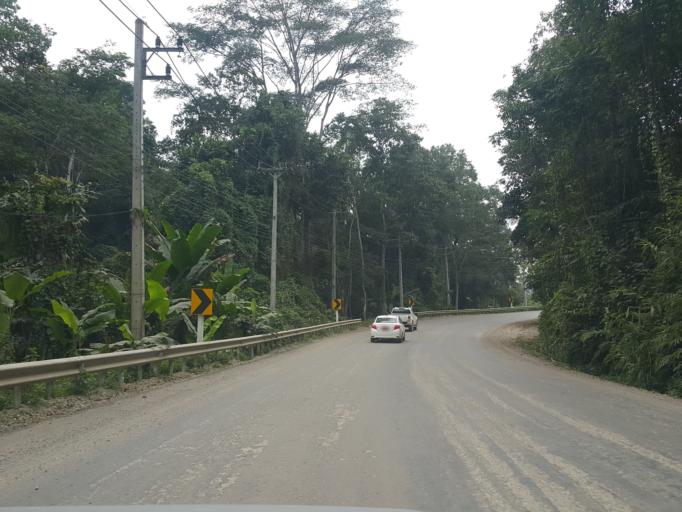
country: TH
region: Chiang Mai
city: Mae Taeng
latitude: 19.1763
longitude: 98.6925
